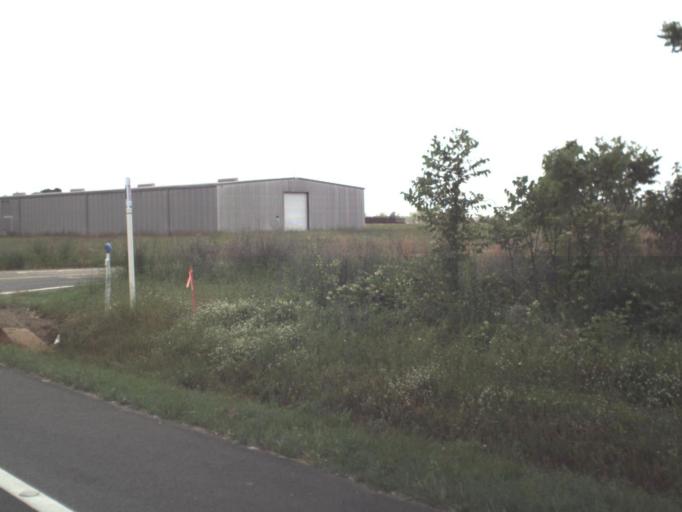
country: US
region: Florida
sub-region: Escambia County
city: Century
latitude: 30.9319
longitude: -87.1574
